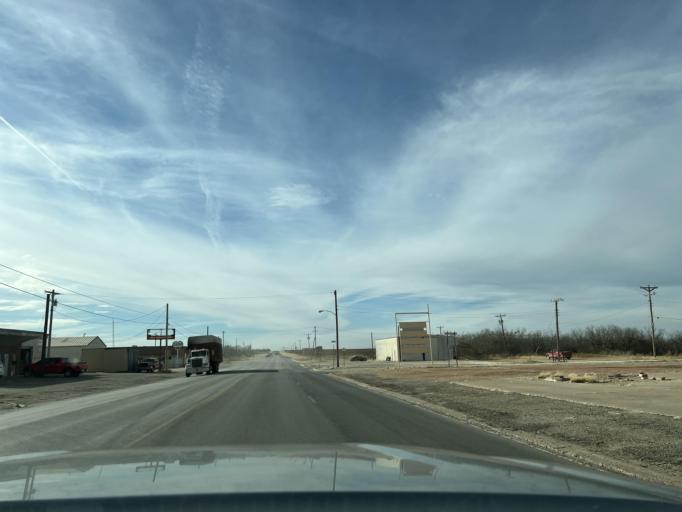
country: US
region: Texas
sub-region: Jones County
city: Anson
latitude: 32.7516
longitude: -99.9032
